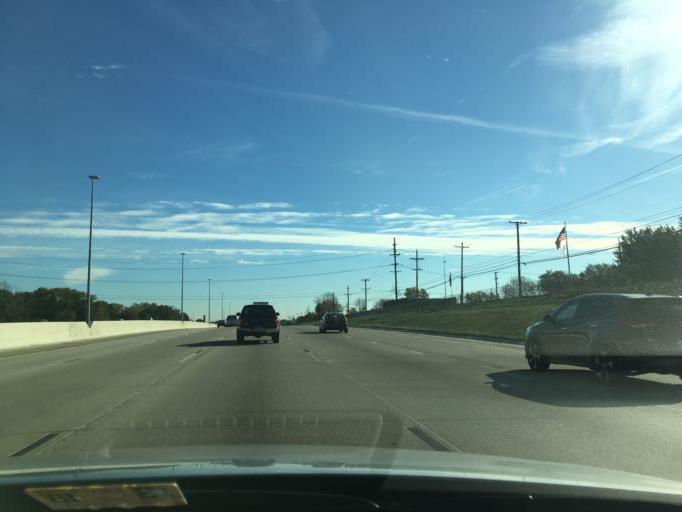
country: US
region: Michigan
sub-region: Wayne County
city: Livonia
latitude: 42.3831
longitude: -83.3457
